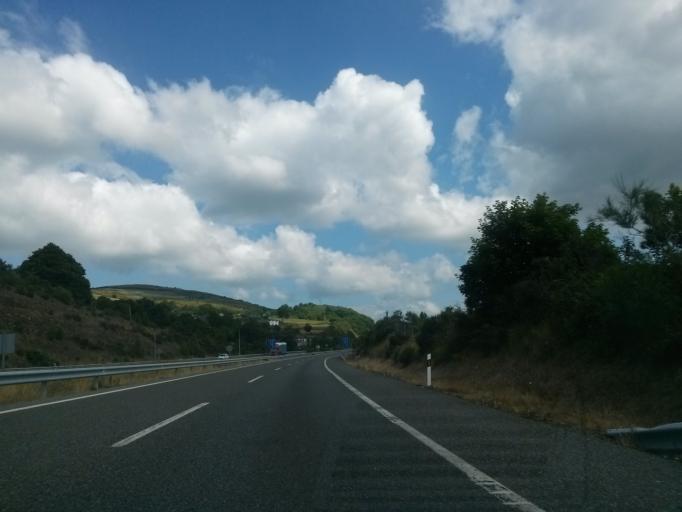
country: ES
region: Galicia
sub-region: Provincia de Lugo
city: Becerrea
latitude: 42.7826
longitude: -7.1031
